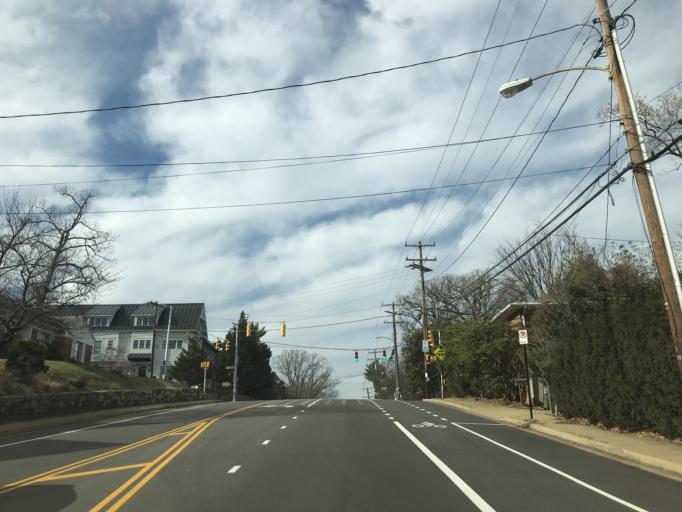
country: US
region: Virginia
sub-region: Arlington County
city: Arlington
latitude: 38.8996
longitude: -77.0978
